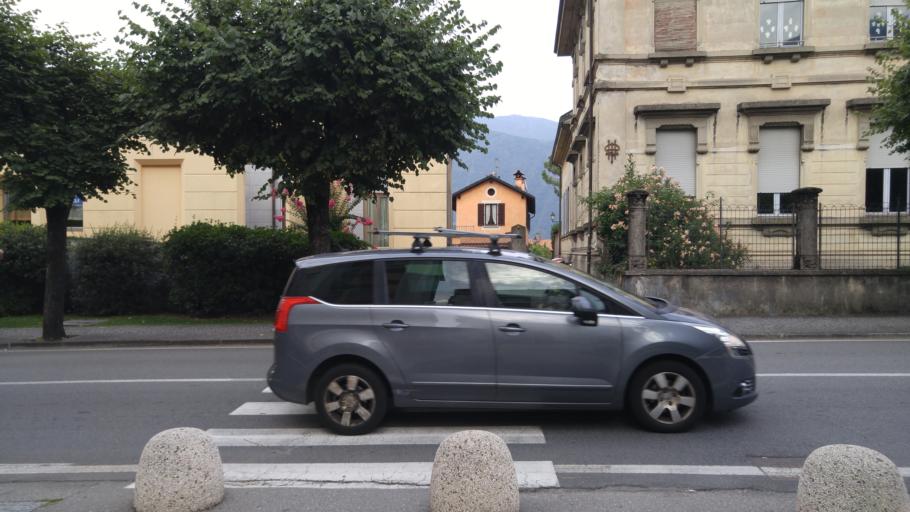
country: IT
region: Piedmont
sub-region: Provincia Verbano-Cusio-Ossola
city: Cannobio
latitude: 46.0626
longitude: 8.6974
